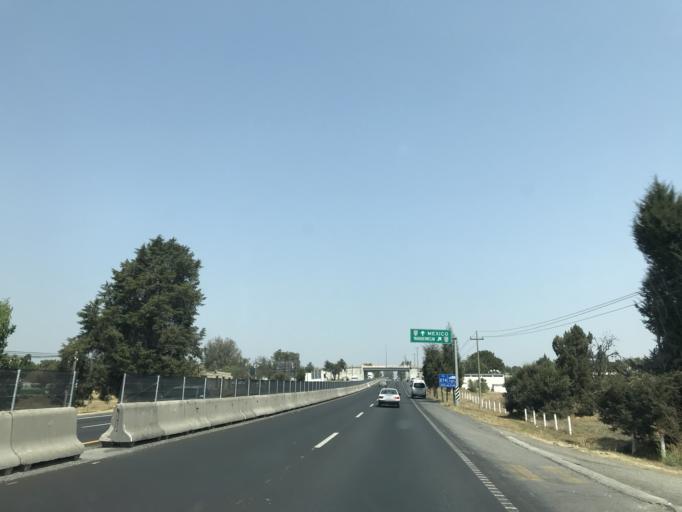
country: MX
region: Tlaxcala
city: Yauhquemehcan
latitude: 19.3999
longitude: -98.1850
